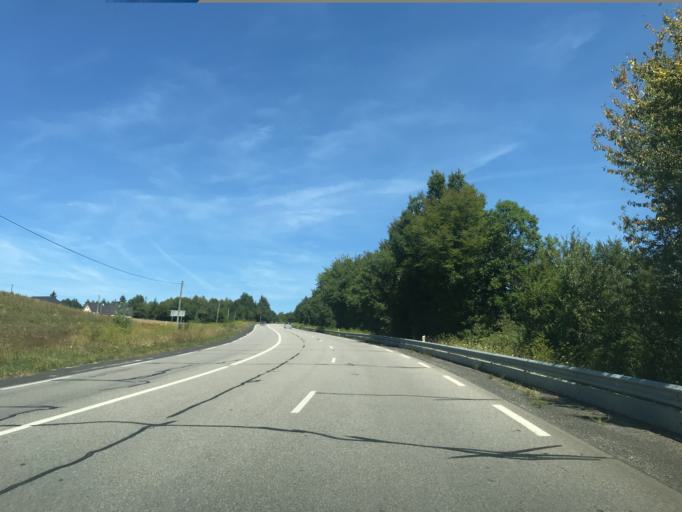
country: FR
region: Limousin
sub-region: Departement de la Correze
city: Naves
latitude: 45.2984
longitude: 1.8151
